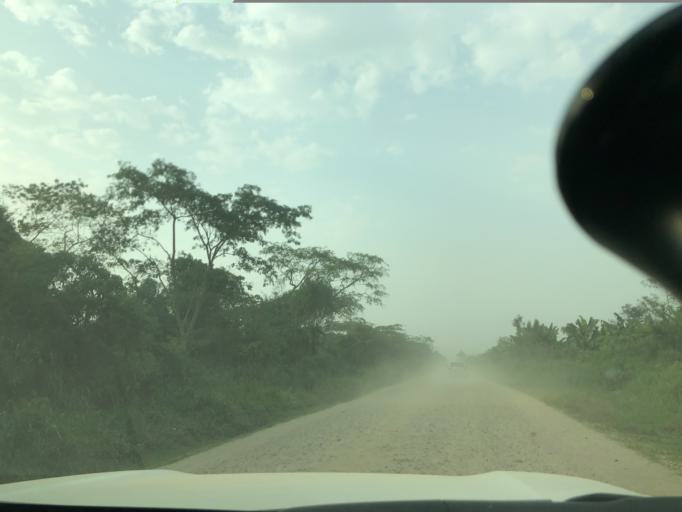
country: UG
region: Western Region
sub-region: Kasese District
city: Margherita
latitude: 0.2650
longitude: 29.6765
